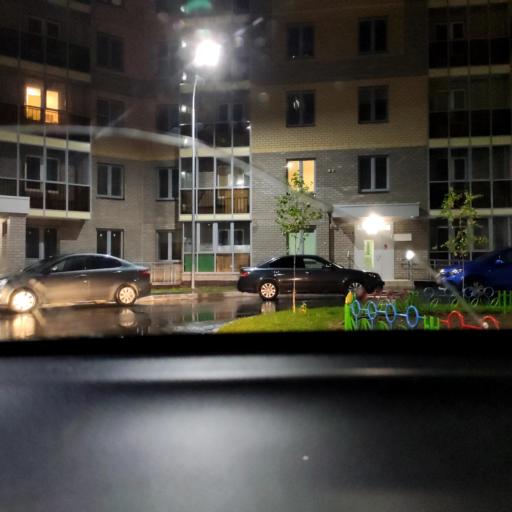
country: RU
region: Tatarstan
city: Staroye Arakchino
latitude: 55.8216
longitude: 49.0348
